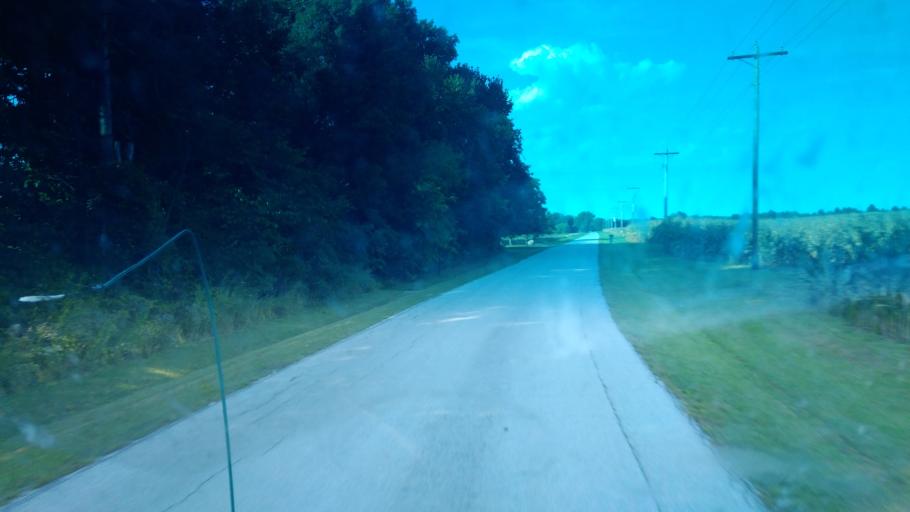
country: US
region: Ohio
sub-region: Wyandot County
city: Carey
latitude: 40.9085
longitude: -83.3571
